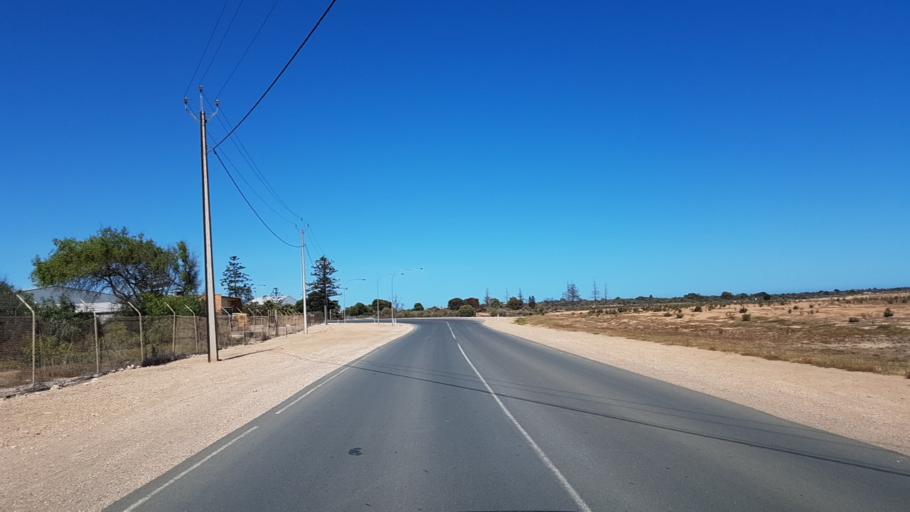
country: AU
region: South Australia
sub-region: Copper Coast
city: Wallaroo
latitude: -33.9353
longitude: 137.6088
